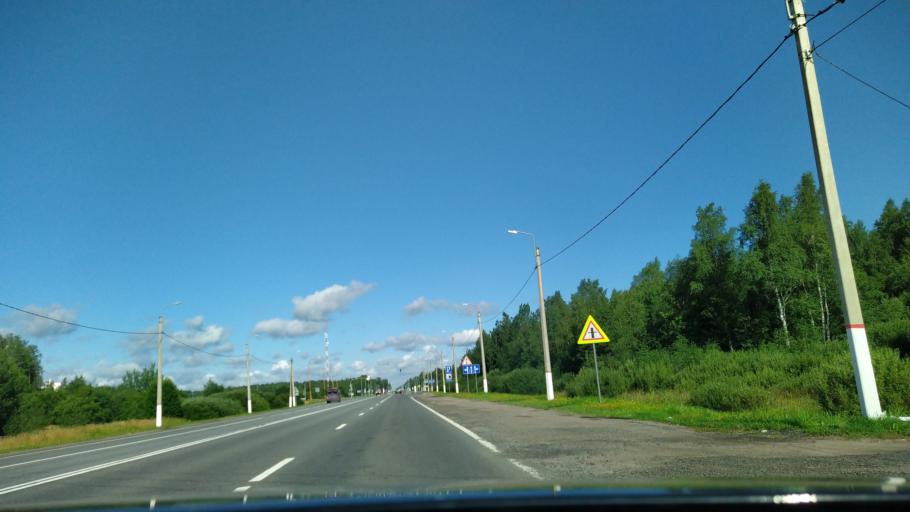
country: RU
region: Leningrad
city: Tosno
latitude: 59.5667
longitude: 30.8302
